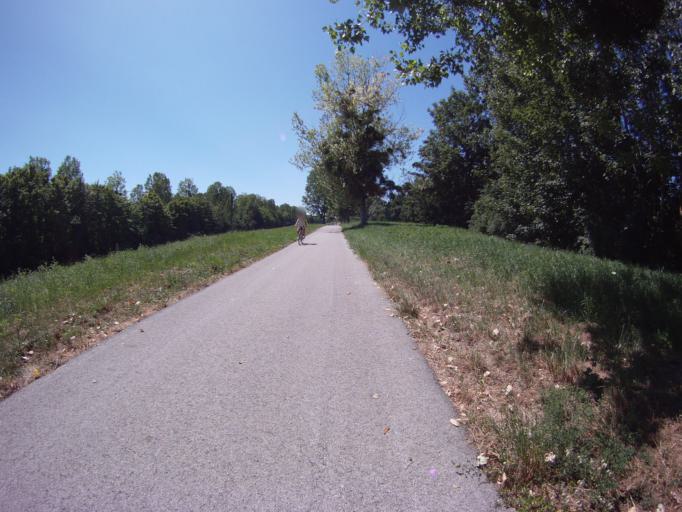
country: FR
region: Champagne-Ardenne
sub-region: Departement de la Marne
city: Damery
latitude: 49.0741
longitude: 3.8553
